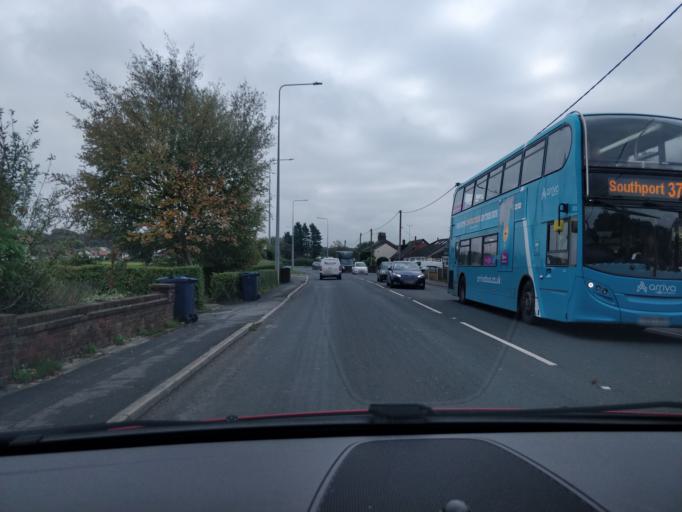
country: GB
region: England
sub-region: Lancashire
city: Ormskirk
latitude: 53.6126
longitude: -2.9395
